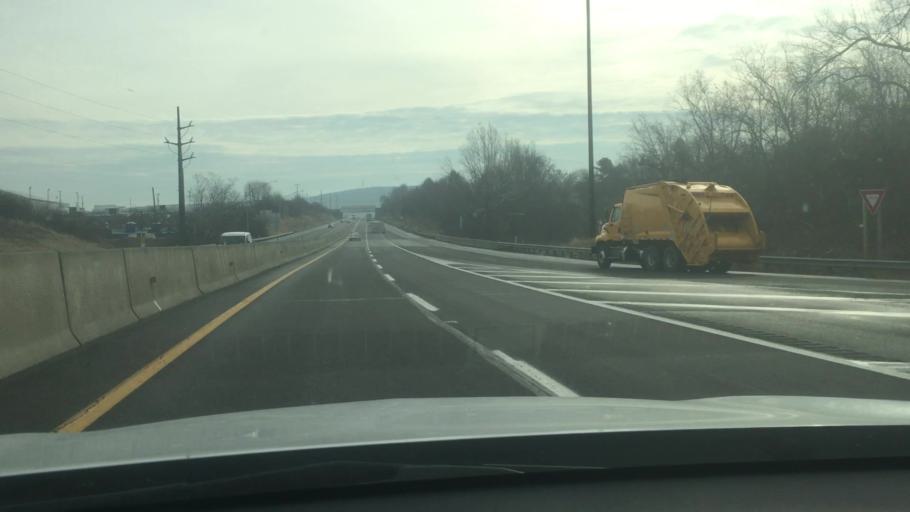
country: US
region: Pennsylvania
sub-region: Chester County
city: Elverson
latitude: 40.1589
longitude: -75.8793
